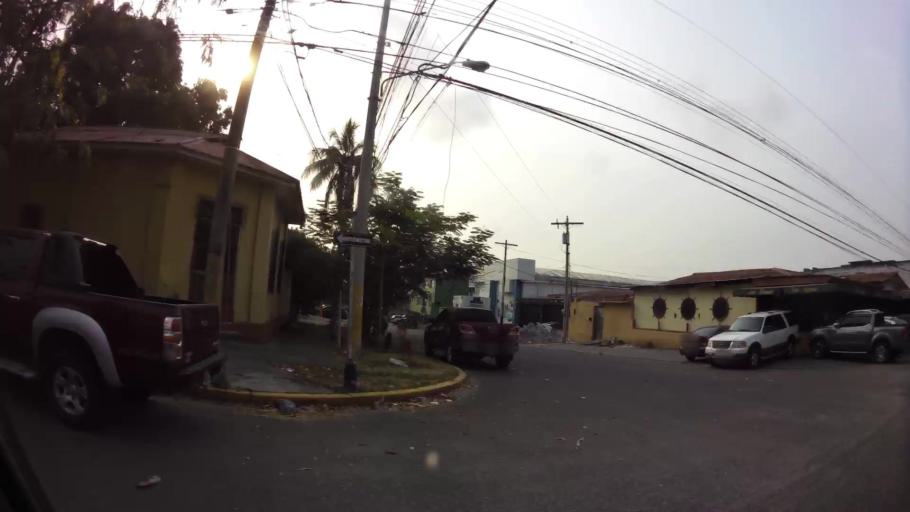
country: HN
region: Cortes
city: San Pedro Sula
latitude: 15.4999
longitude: -88.0358
